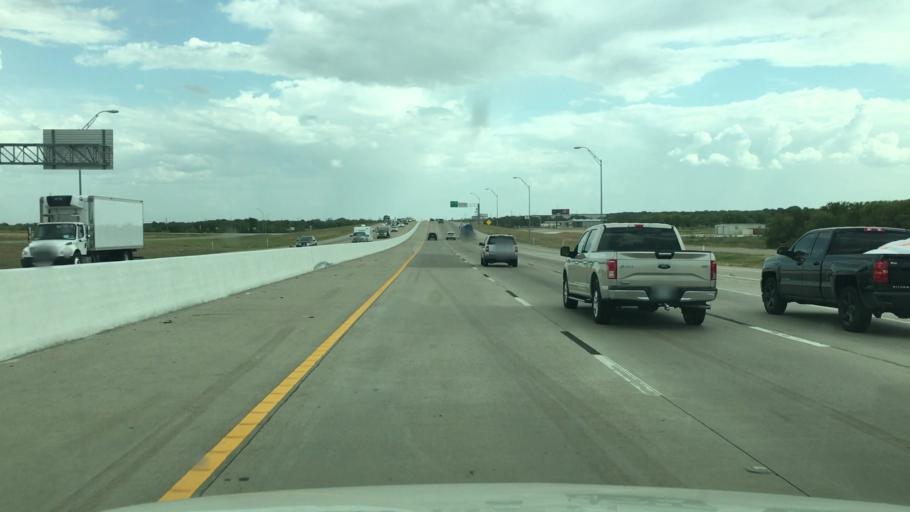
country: US
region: Texas
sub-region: McLennan County
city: West
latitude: 31.7331
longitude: -97.1033
